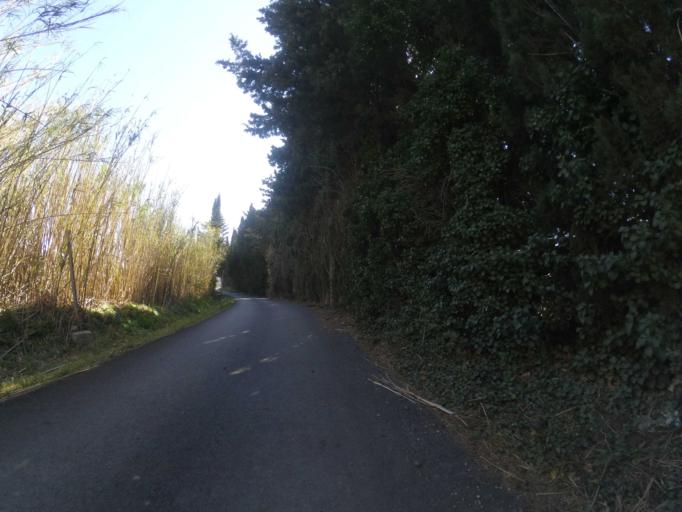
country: FR
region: Languedoc-Roussillon
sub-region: Departement des Pyrenees-Orientales
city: Corneilla-la-Riviere
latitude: 42.6831
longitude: 2.7172
